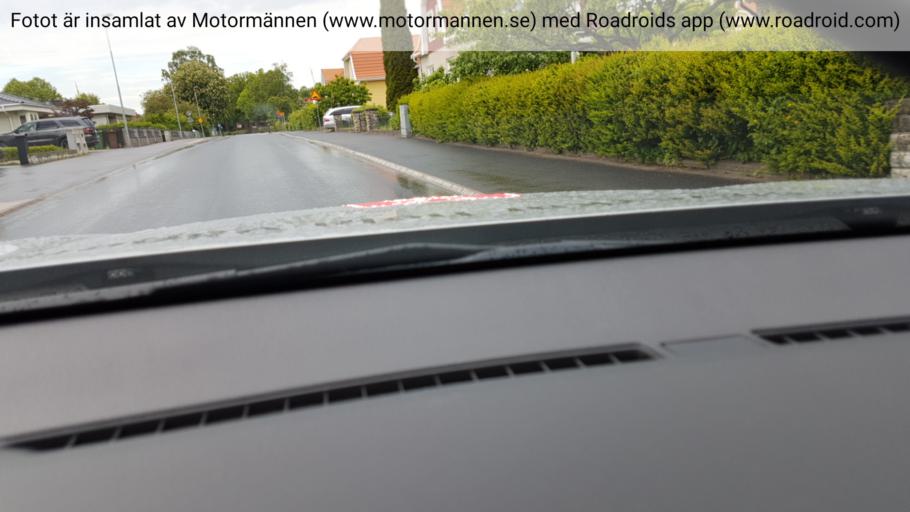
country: SE
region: Vaestra Goetaland
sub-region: Skovde Kommun
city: Skoevde
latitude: 58.3983
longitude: 13.8543
